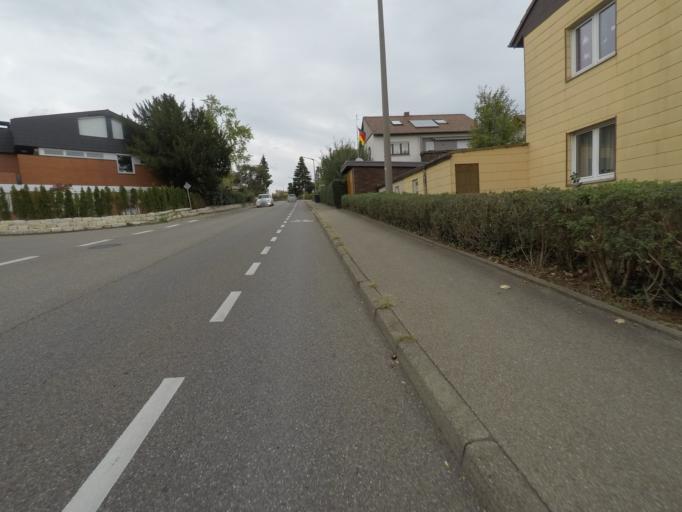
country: DE
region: Baden-Wuerttemberg
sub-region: Regierungsbezirk Stuttgart
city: Schlaitdorf
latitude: 48.6253
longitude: 9.2355
